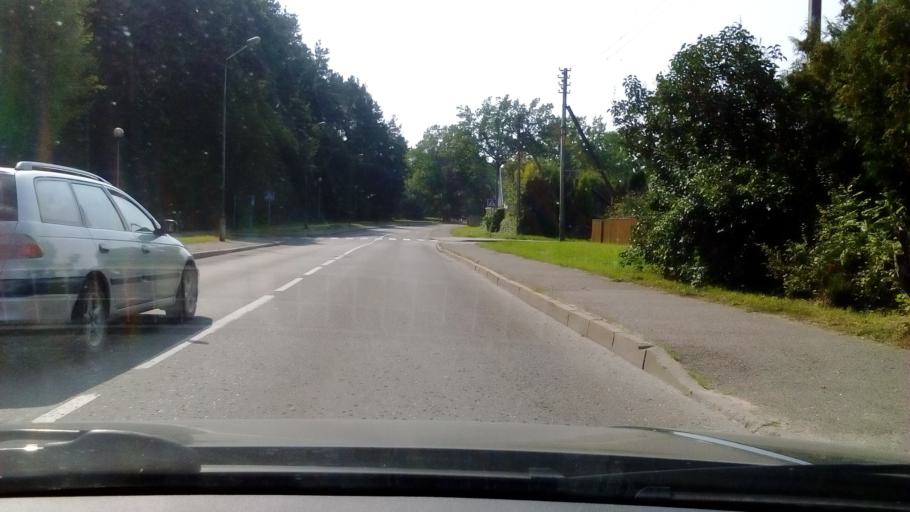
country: LT
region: Alytaus apskritis
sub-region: Alytus
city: Alytus
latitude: 54.3856
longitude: 24.0619
